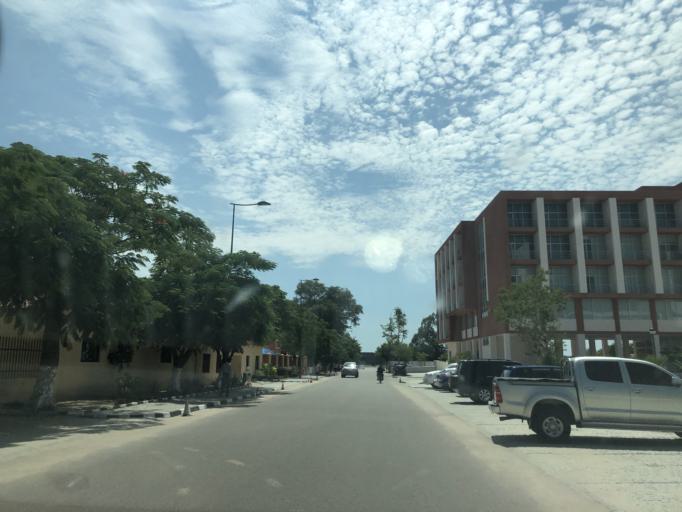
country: AO
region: Cunene
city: Ondjiva
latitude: -17.0662
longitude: 15.7265
